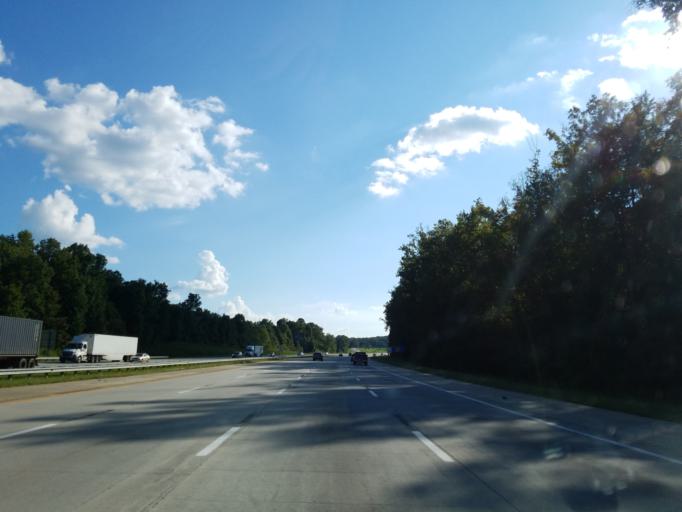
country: US
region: North Carolina
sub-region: Rowan County
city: East Spencer
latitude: 35.6832
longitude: -80.4076
